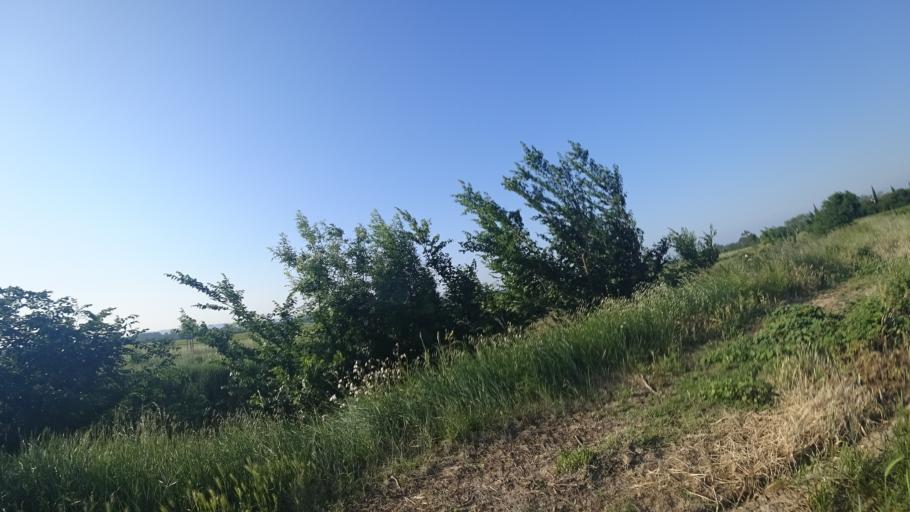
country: FR
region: Languedoc-Roussillon
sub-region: Departement de l'Aude
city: Canet
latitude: 43.2503
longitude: 2.8079
